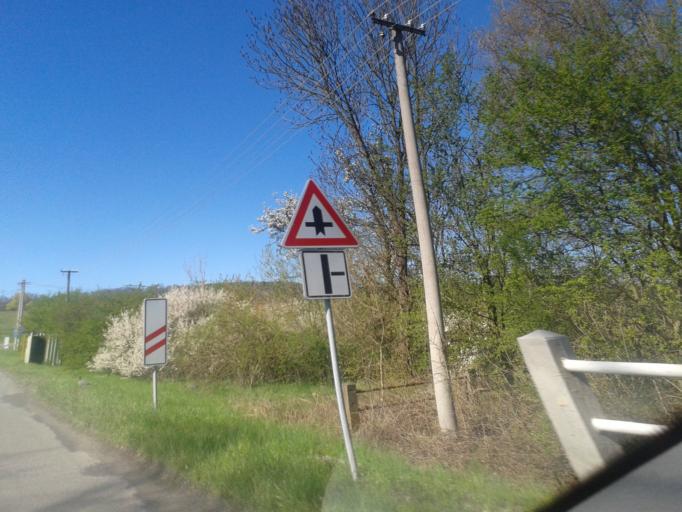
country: CZ
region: Central Bohemia
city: Revnice
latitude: 49.8874
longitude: 14.1491
